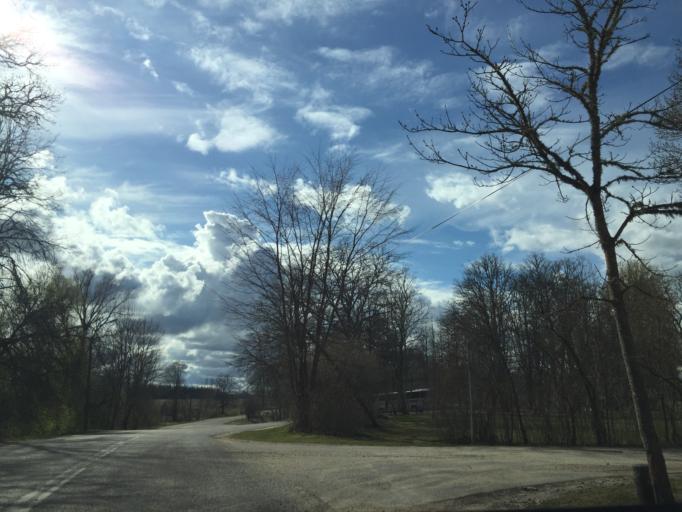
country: LV
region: Burtnieki
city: Matisi
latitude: 57.5969
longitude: 25.0743
